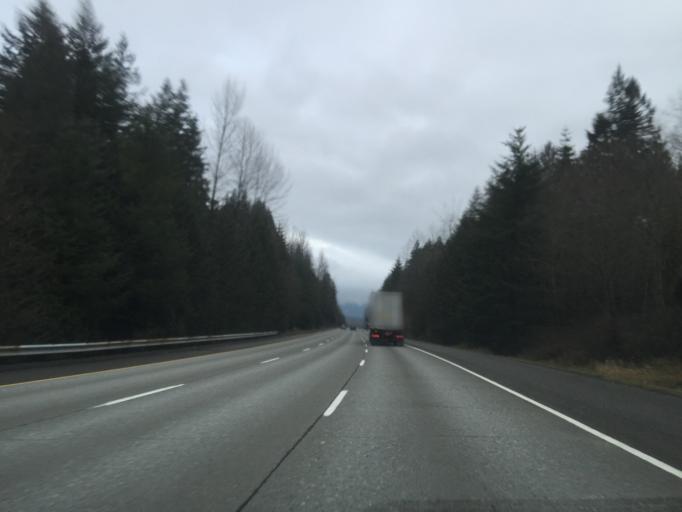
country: US
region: Washington
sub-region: King County
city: North Bend
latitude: 47.4945
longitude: -121.8119
